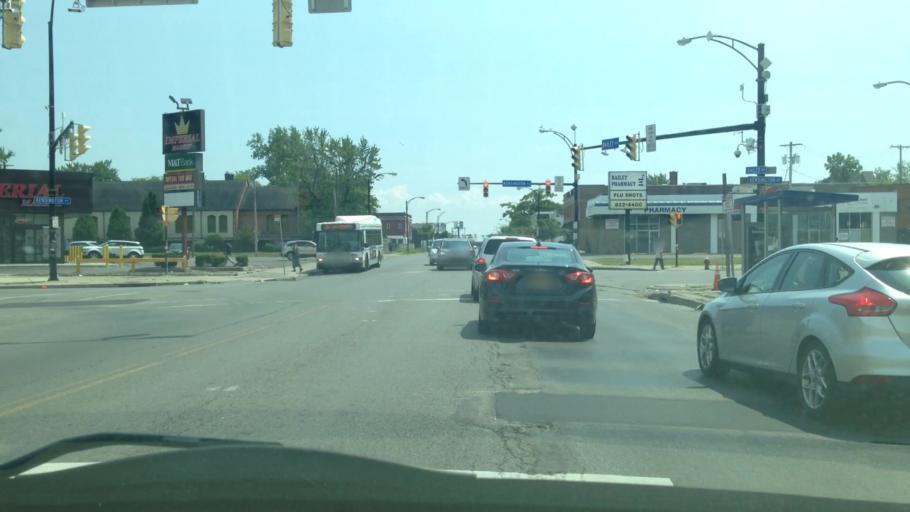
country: US
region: New York
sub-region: Erie County
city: Eggertsville
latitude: 42.9383
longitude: -78.8137
